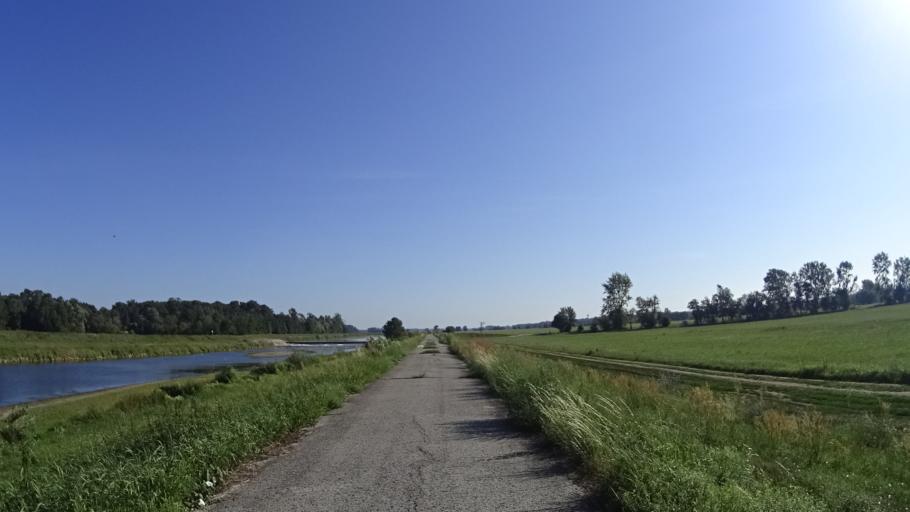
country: CZ
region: South Moravian
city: Tvrdonice
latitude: 48.7325
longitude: 17.0194
